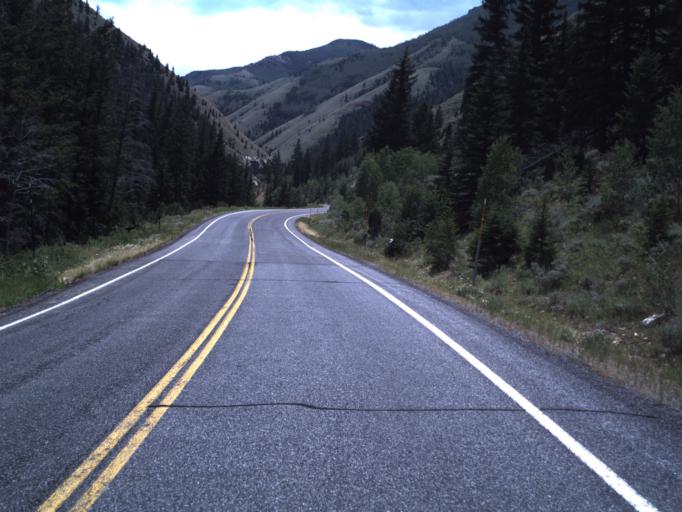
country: US
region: Utah
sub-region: Emery County
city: Huntington
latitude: 39.4867
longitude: -111.1588
